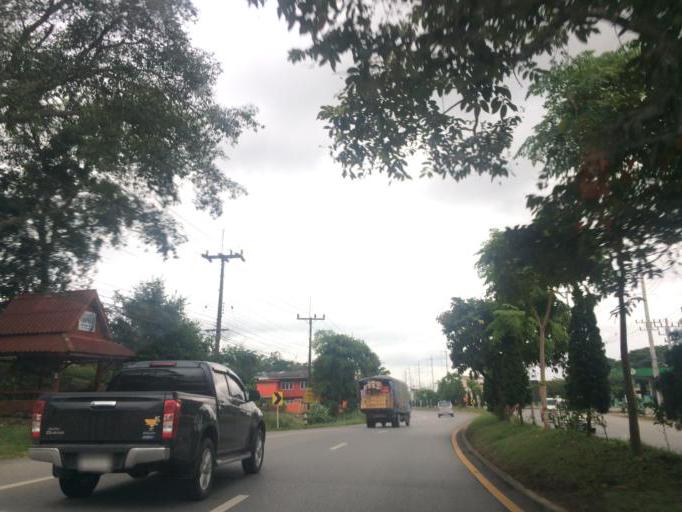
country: TH
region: Chiang Rai
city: Mae Chan
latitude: 20.1296
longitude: 99.8646
